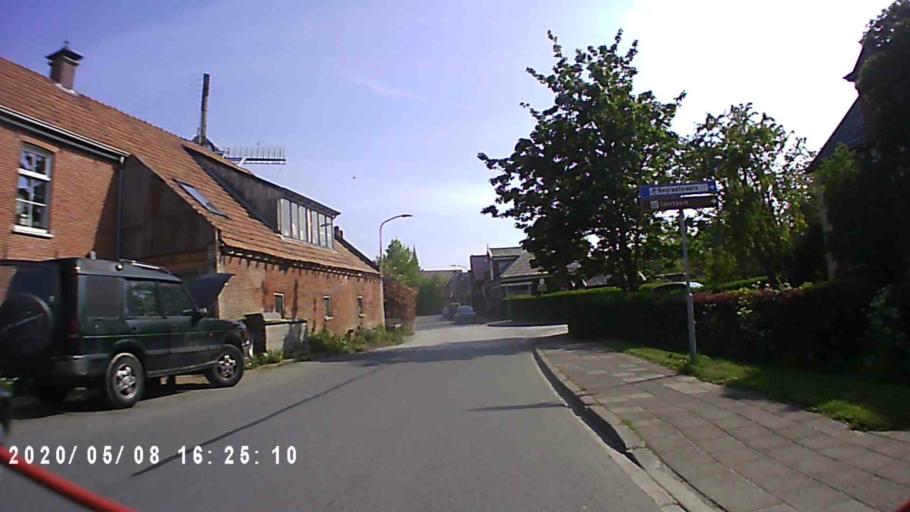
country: NL
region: Groningen
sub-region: Gemeente Bedum
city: Bedum
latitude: 53.3678
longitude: 6.6347
